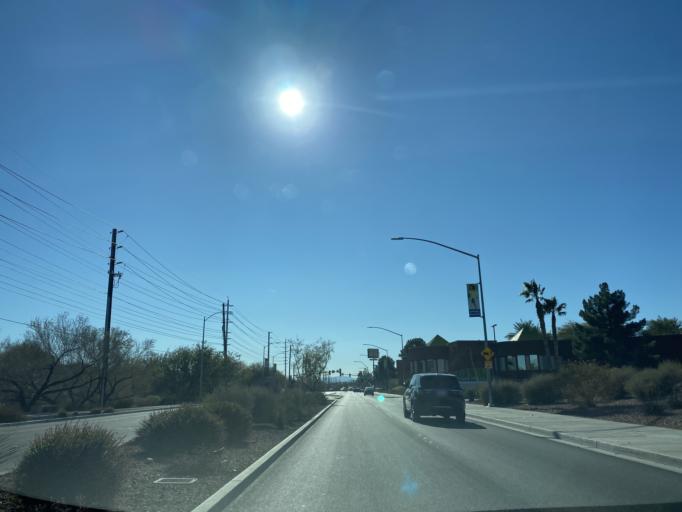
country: US
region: Nevada
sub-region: Clark County
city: Las Vegas
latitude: 36.1719
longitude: -115.1927
